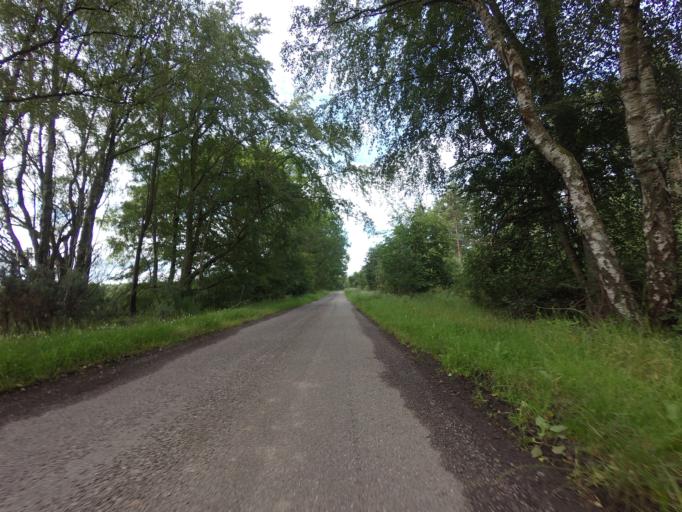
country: GB
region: Scotland
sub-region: Moray
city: Hopeman
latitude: 57.6685
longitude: -3.4189
